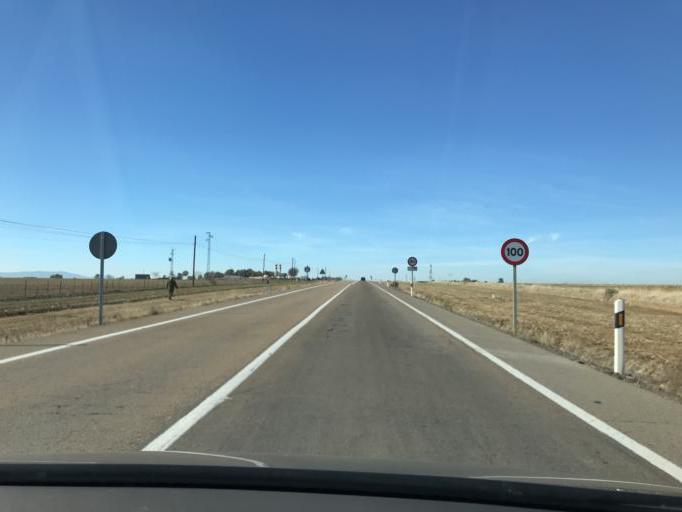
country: ES
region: Extremadura
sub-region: Provincia de Badajoz
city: Azuaga
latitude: 38.2604
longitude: -5.7029
